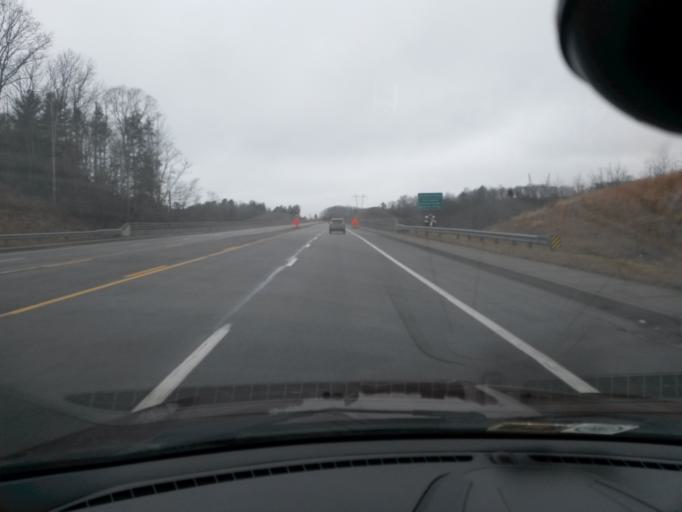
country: US
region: West Virginia
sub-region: Raleigh County
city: Stanaford
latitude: 37.7898
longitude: -81.1626
